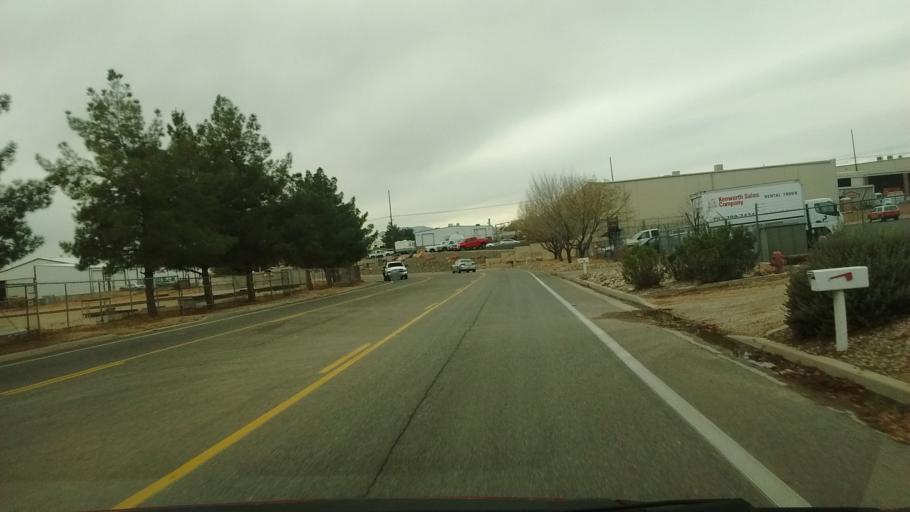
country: US
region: Utah
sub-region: Washington County
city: Washington
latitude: 37.1152
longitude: -113.5113
